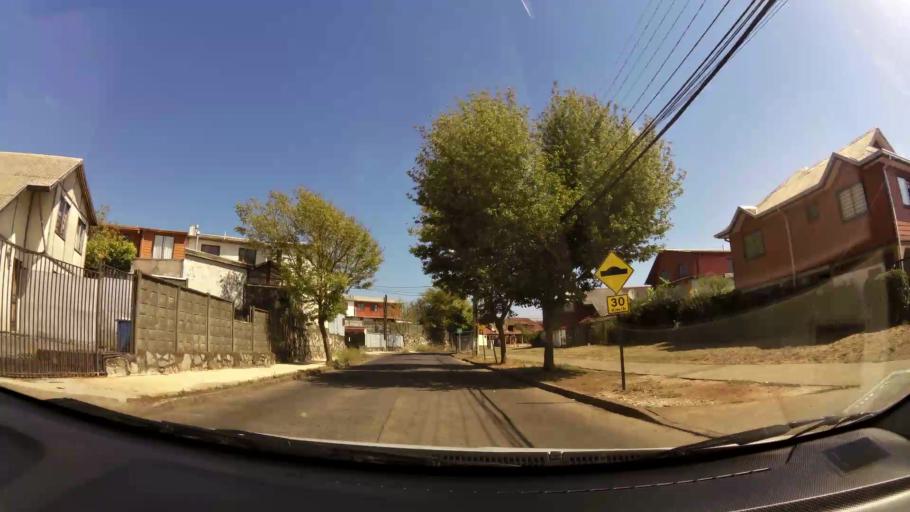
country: CL
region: Biobio
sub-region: Provincia de Concepcion
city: Concepcion
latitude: -36.7791
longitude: -73.0406
